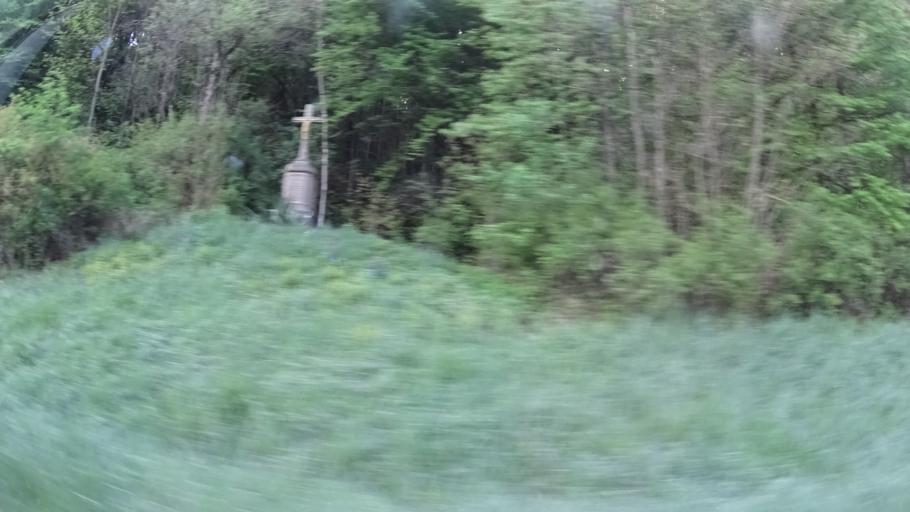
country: DE
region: Baden-Wuerttemberg
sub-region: Tuebingen Region
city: Haigerloch
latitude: 48.4091
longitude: 8.7702
